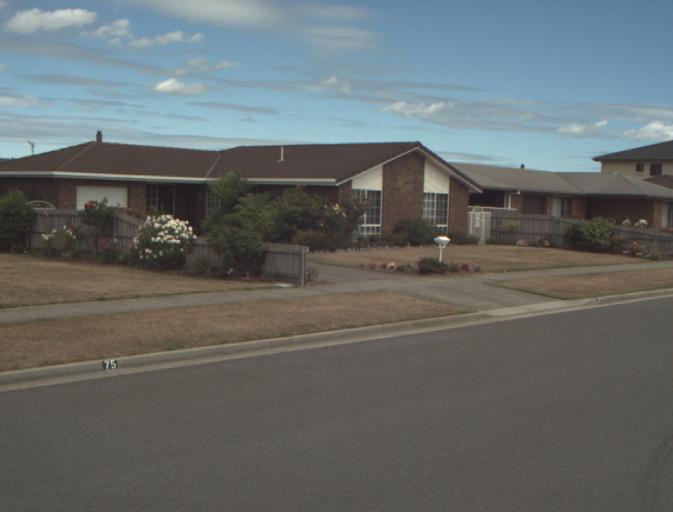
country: AU
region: Tasmania
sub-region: Launceston
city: Invermay
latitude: -41.3903
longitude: 147.1144
